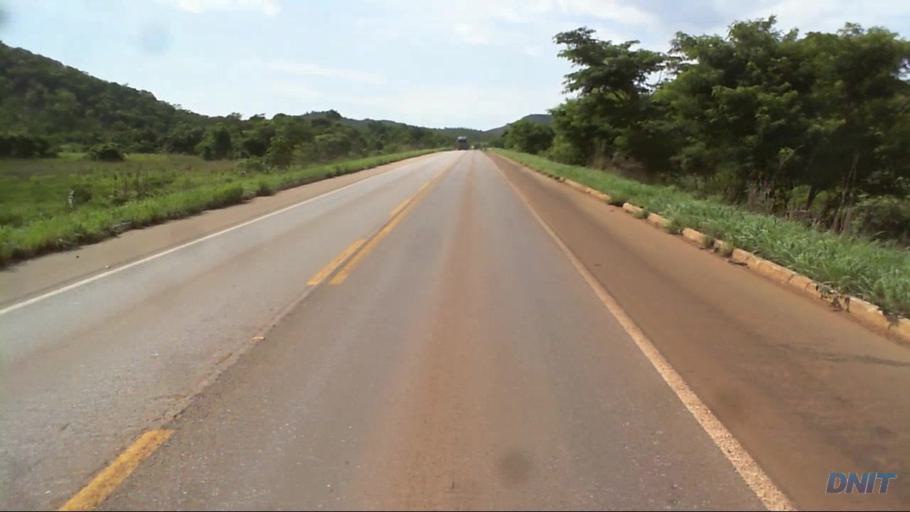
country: BR
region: Goias
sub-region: Barro Alto
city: Barro Alto
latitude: -15.1244
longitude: -48.8364
